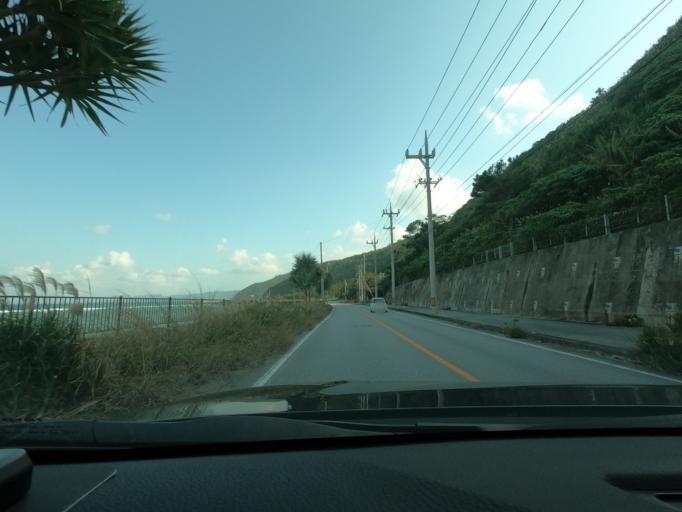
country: JP
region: Okinawa
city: Nago
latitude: 26.7636
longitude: 128.1938
